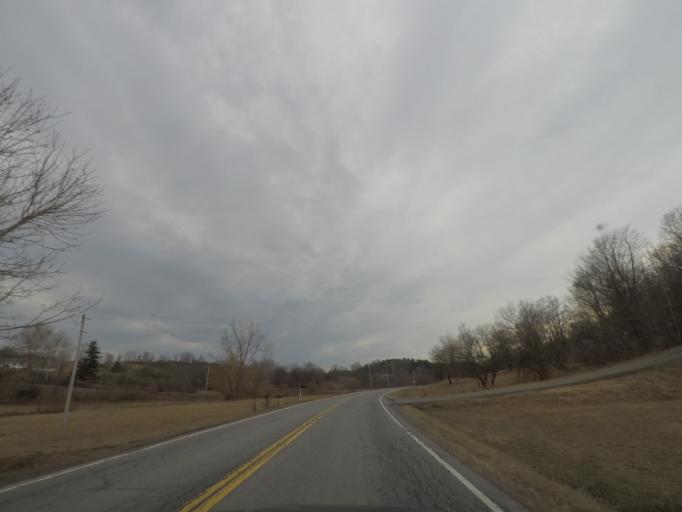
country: US
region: New York
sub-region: Washington County
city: Greenwich
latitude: 43.0736
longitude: -73.4956
